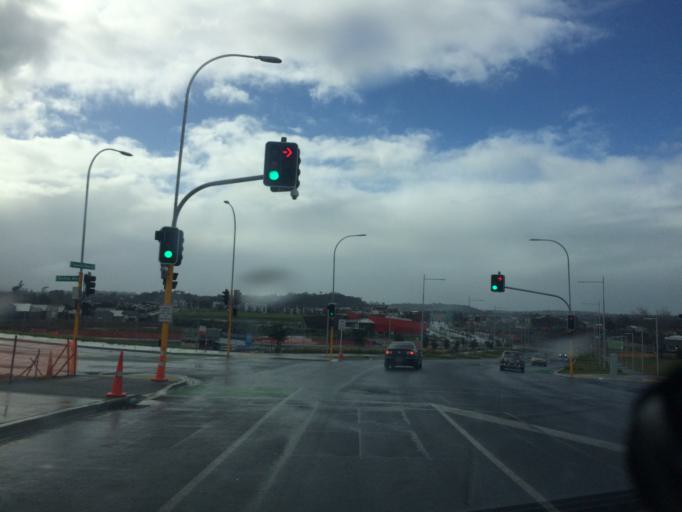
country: NZ
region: Auckland
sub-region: Auckland
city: Rosebank
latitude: -36.7969
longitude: 174.6501
